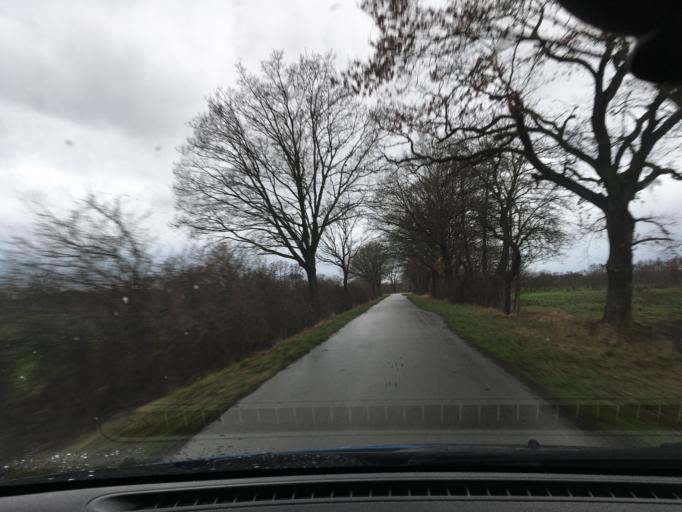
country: DE
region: Lower Saxony
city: Hittbergen
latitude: 53.3243
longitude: 10.6479
